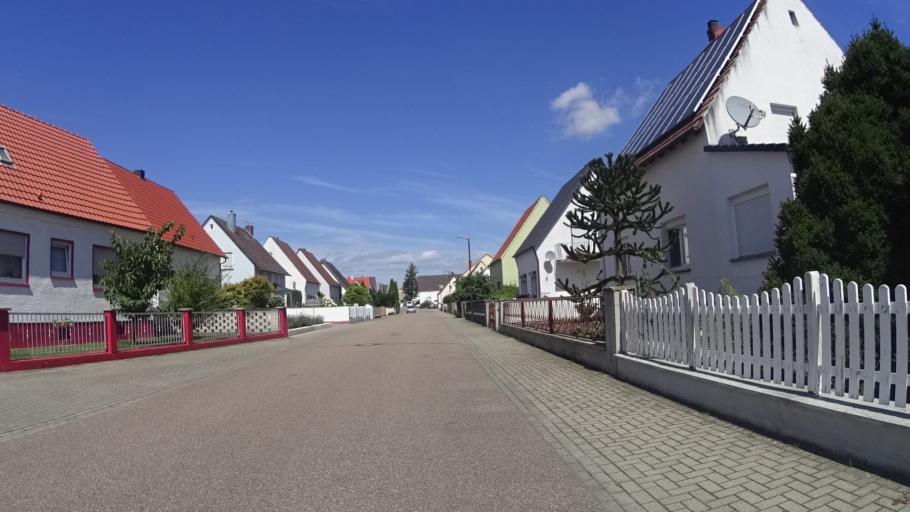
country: DE
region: Rheinland-Pfalz
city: Lingenfeld
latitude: 49.2417
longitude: 8.3548
